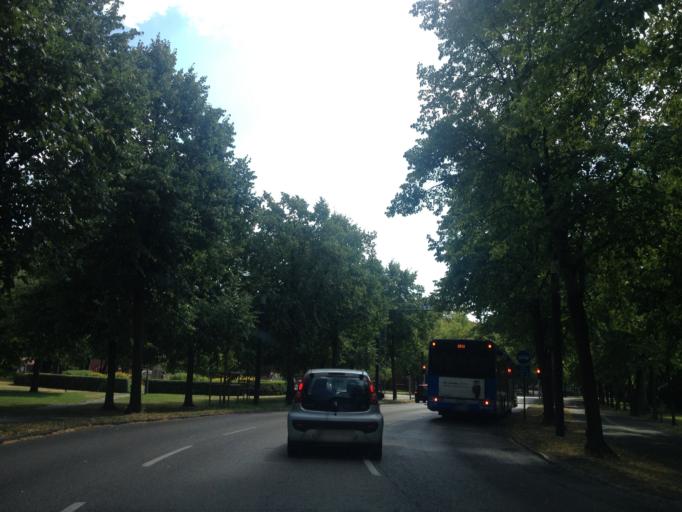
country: SE
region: Vaestra Goetaland
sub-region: Goteborg
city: Goeteborg
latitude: 57.7058
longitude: 11.9778
